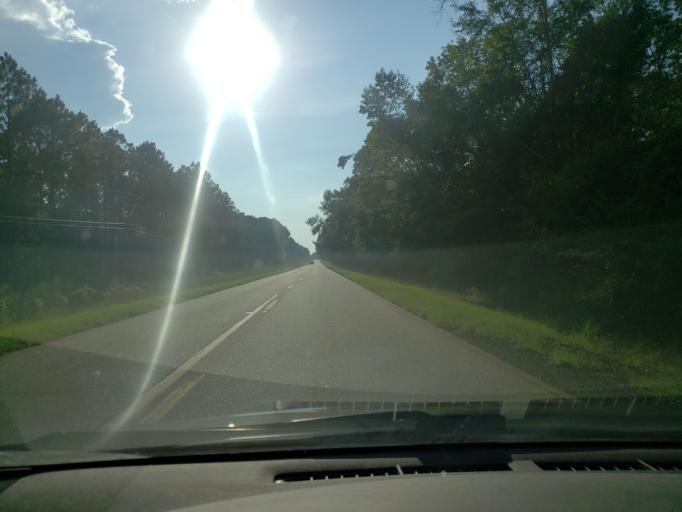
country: US
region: Georgia
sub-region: Dougherty County
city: Albany
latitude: 31.5746
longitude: -84.3439
